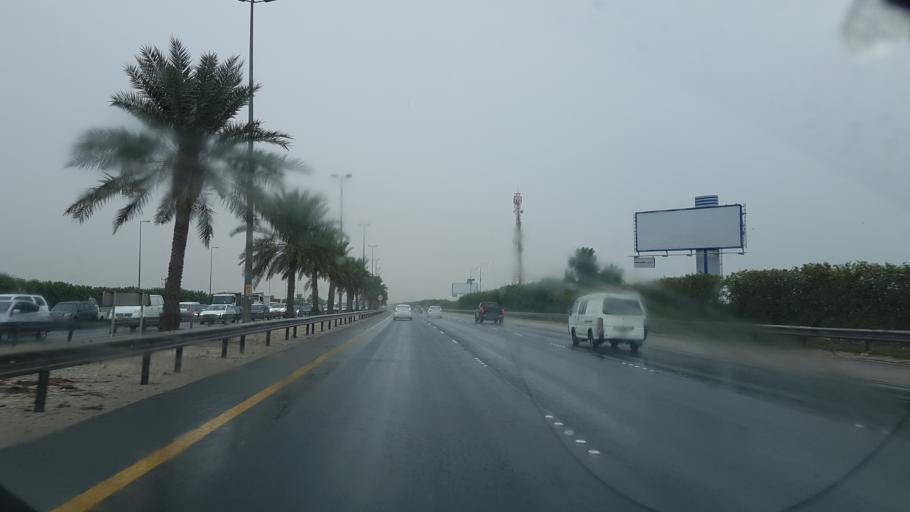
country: BH
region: Northern
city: Madinat `Isa
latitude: 26.1690
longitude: 50.5029
